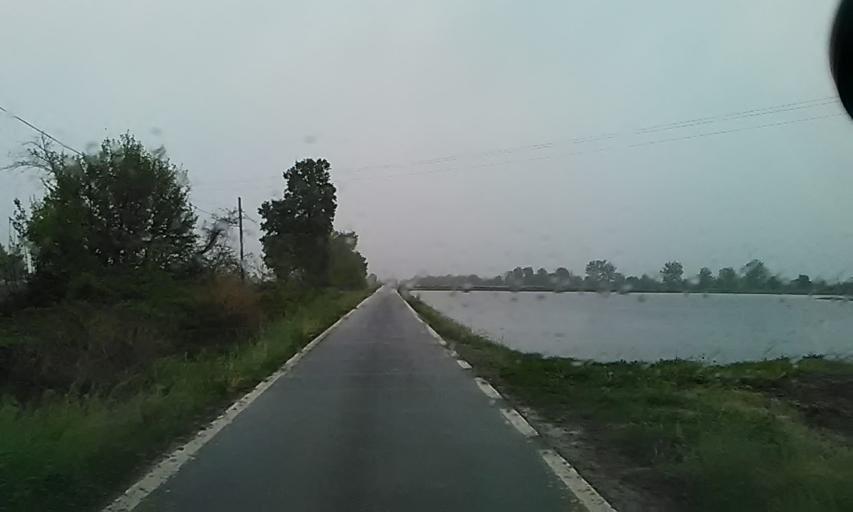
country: IT
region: Piedmont
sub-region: Provincia di Vercelli
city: San Giacomo Vercellese
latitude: 45.4960
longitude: 8.3353
